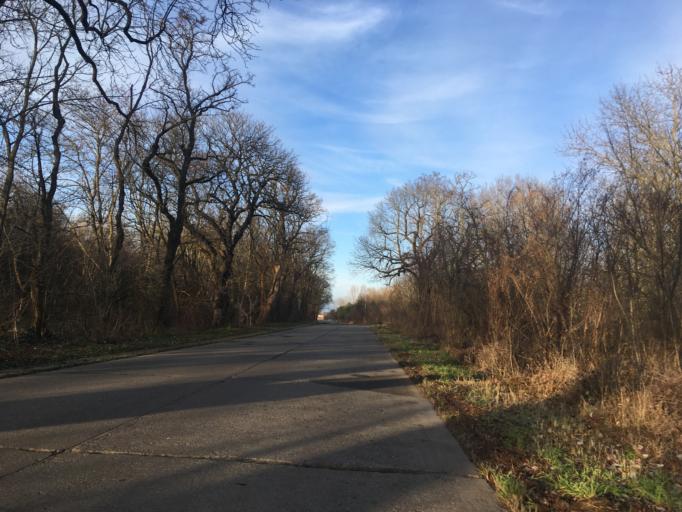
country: DE
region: Berlin
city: Blankenfelde
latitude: 52.6312
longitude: 13.4008
